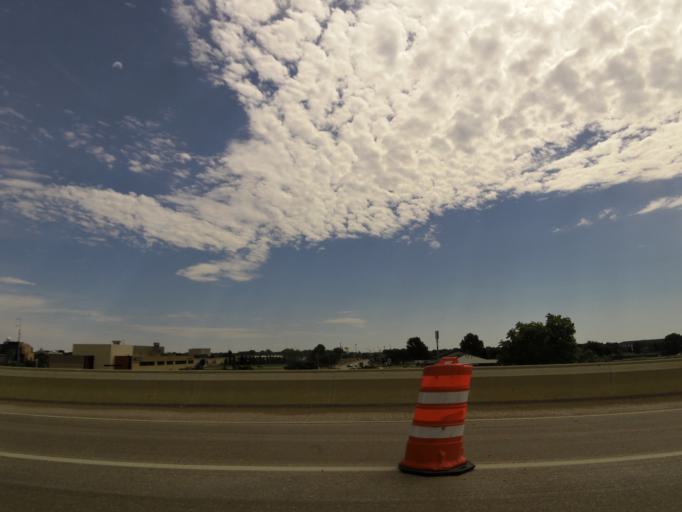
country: US
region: North Dakota
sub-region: Grand Forks County
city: Grand Forks
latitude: 47.9181
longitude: -97.0934
